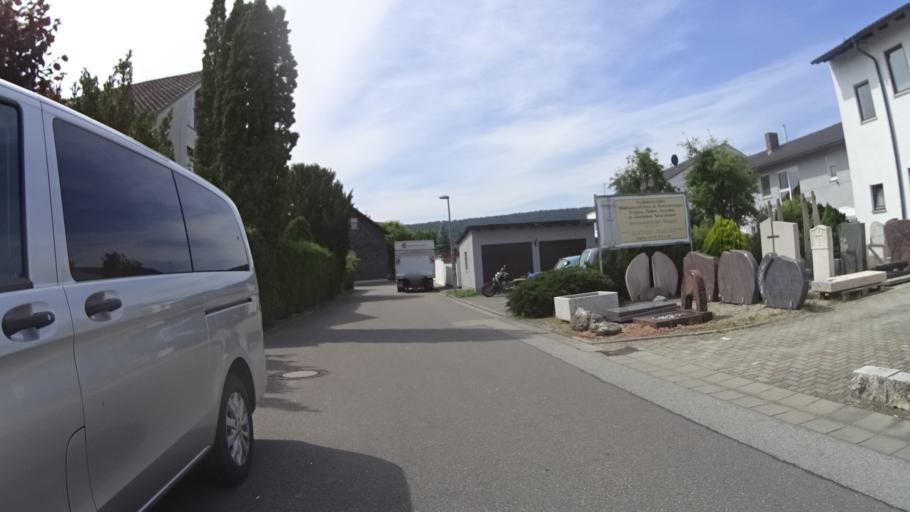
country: DE
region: Bavaria
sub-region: Lower Bavaria
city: Kelheim
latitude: 48.9200
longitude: 11.8826
